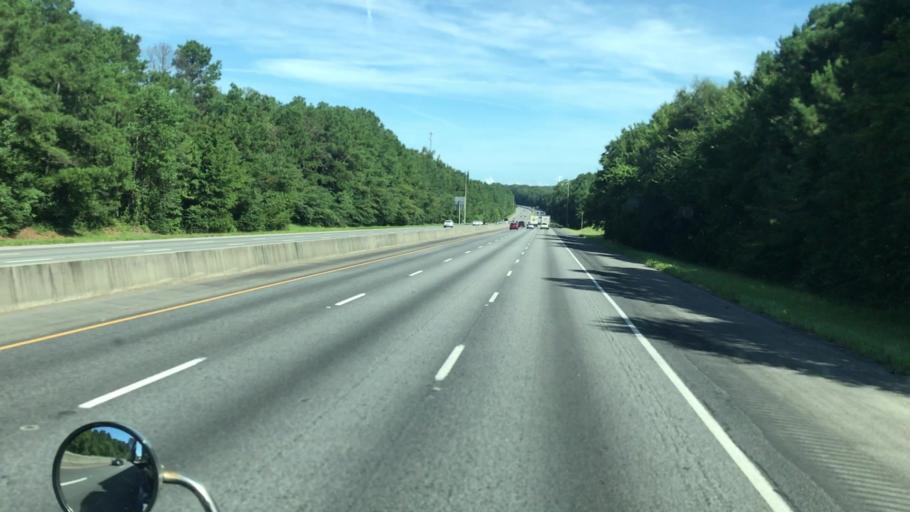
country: US
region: Georgia
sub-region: Bibb County
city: West Point
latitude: 32.8464
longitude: -83.7392
